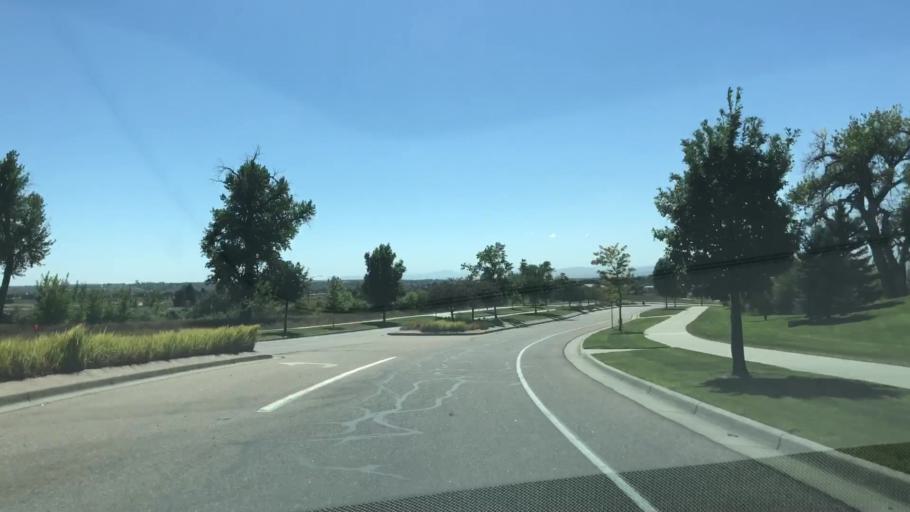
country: US
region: Colorado
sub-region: Weld County
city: Windsor
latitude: 40.5255
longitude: -104.9532
